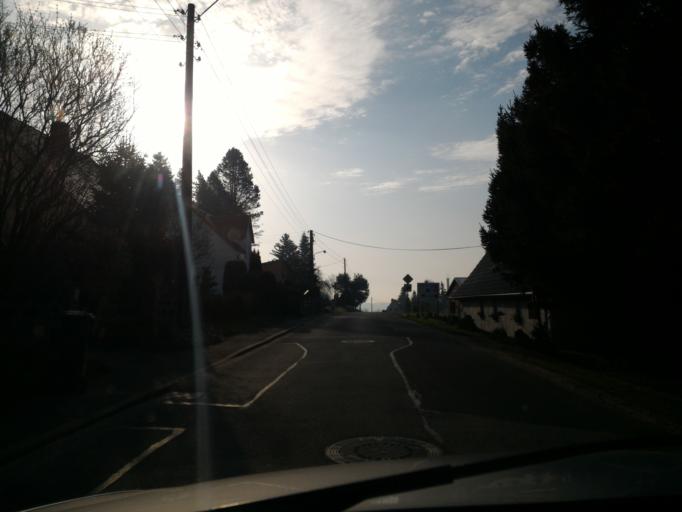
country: DE
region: Saxony
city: Leutersdorf
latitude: 50.9480
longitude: 14.6785
